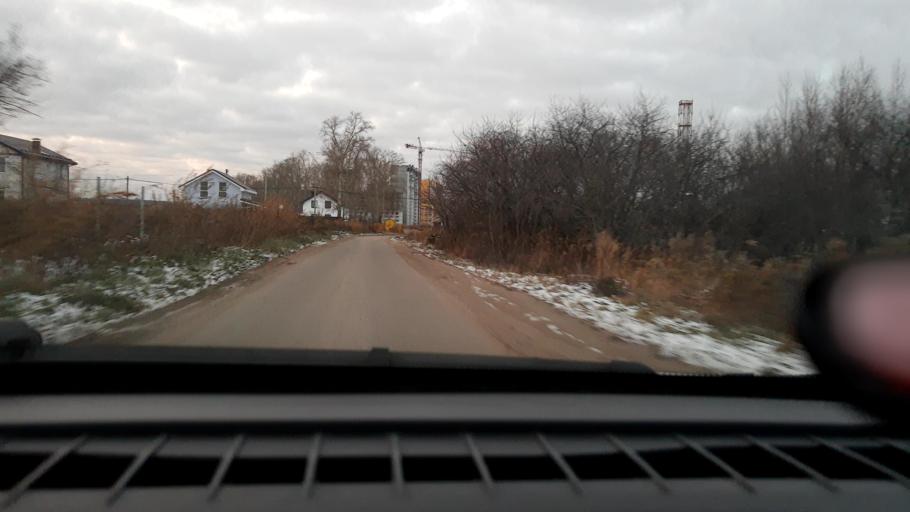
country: RU
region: Nizjnij Novgorod
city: Afonino
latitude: 56.2671
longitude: 44.0523
